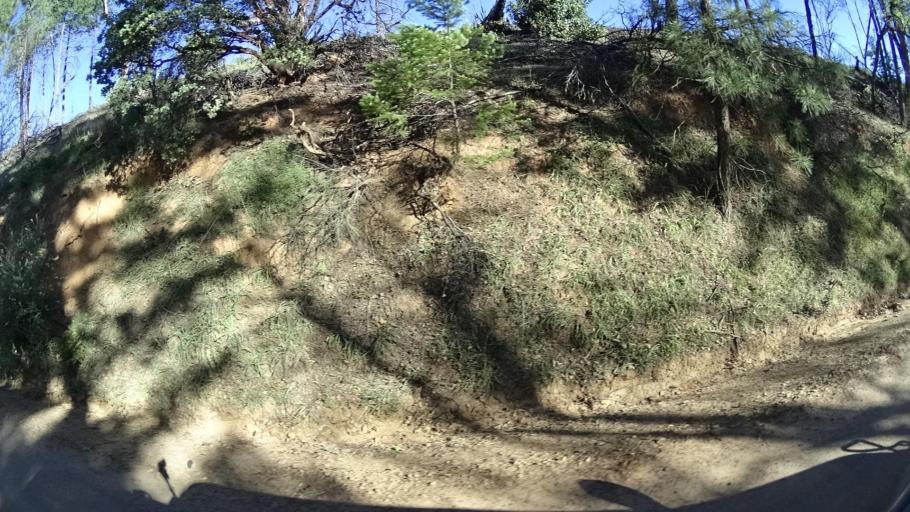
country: US
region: California
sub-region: Lake County
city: Upper Lake
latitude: 39.3895
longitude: -122.9794
